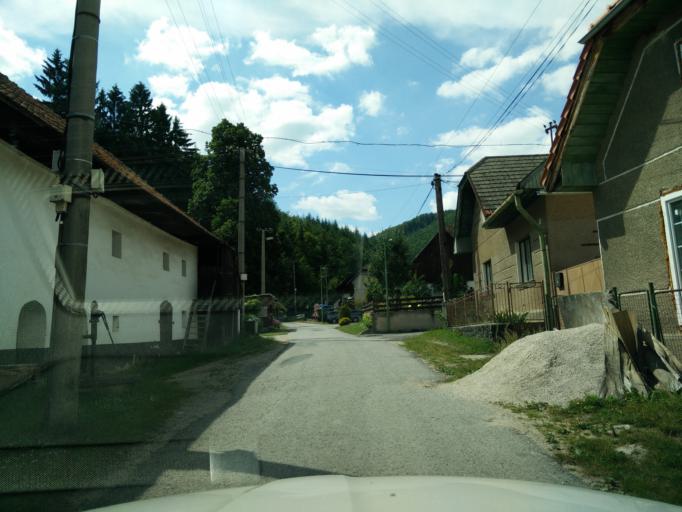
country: SK
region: Nitriansky
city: Bojnice
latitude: 48.8351
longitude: 18.5847
